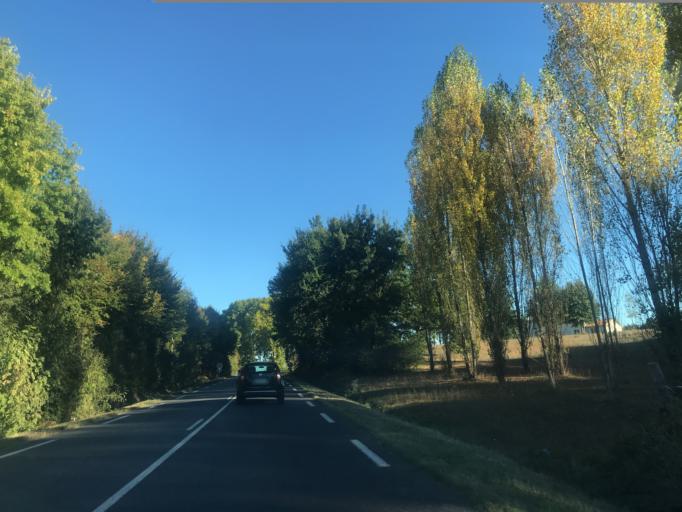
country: FR
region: Poitou-Charentes
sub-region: Departement de la Charente-Maritime
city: Montguyon
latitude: 45.2213
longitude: -0.1983
